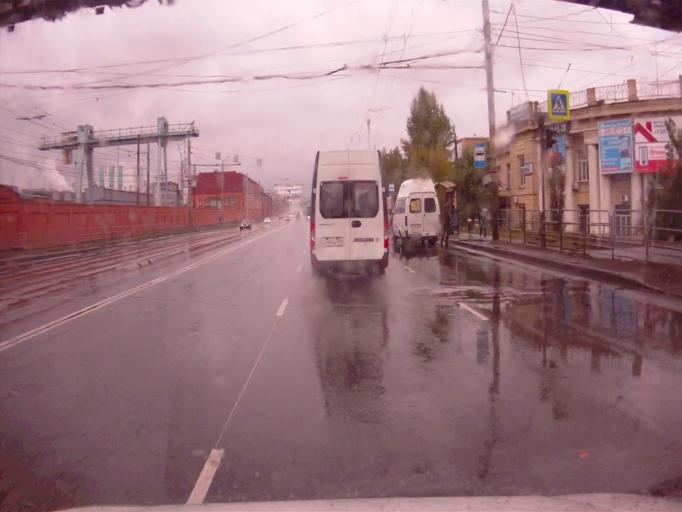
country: RU
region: Chelyabinsk
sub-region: Gorod Chelyabinsk
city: Chelyabinsk
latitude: 55.2055
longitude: 61.3850
